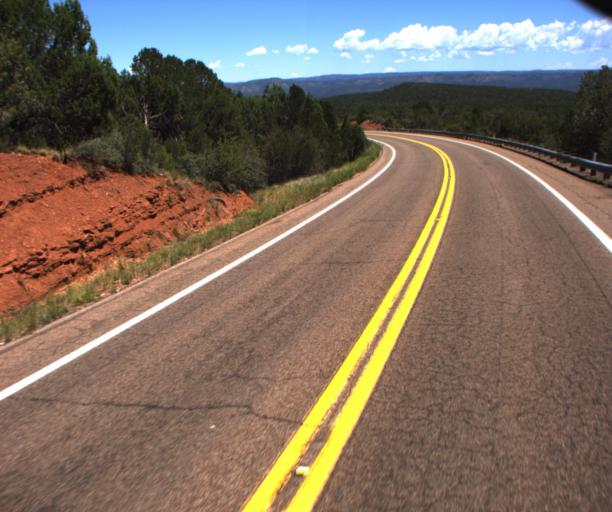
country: US
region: Arizona
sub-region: Navajo County
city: Cibecue
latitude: 33.9316
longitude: -110.3425
